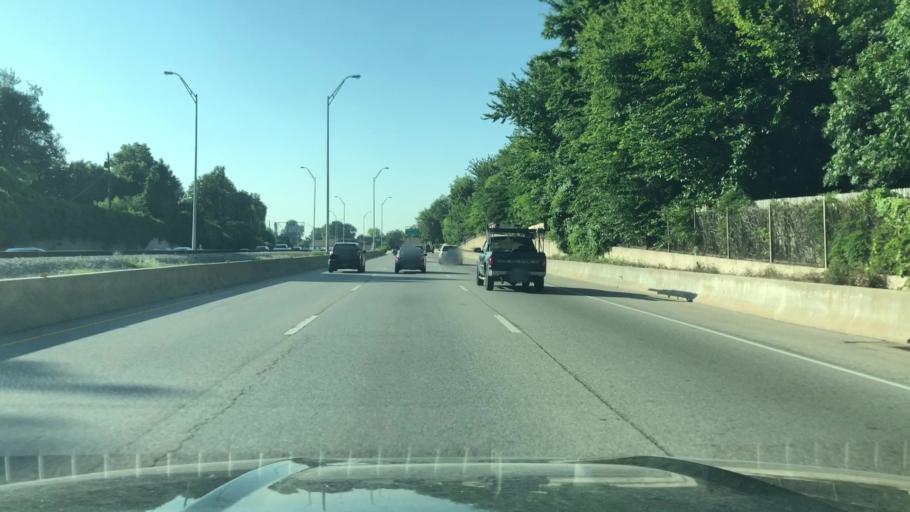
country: US
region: Oklahoma
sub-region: Tulsa County
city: Tulsa
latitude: 36.1303
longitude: -95.9470
